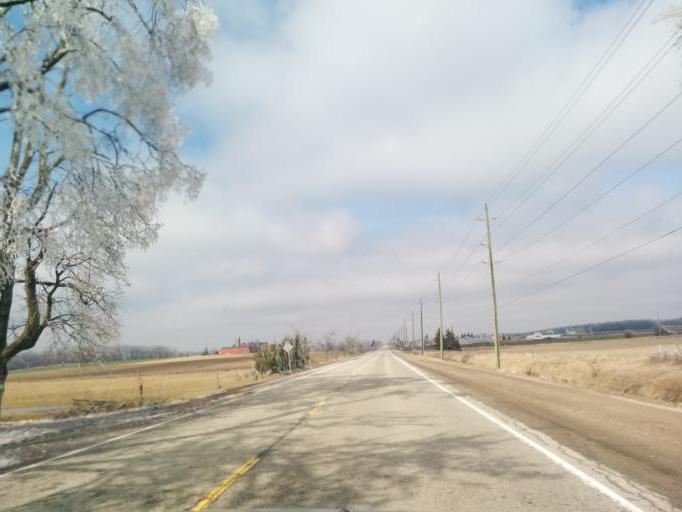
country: CA
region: Ontario
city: Waterloo
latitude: 43.6252
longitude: -80.5514
